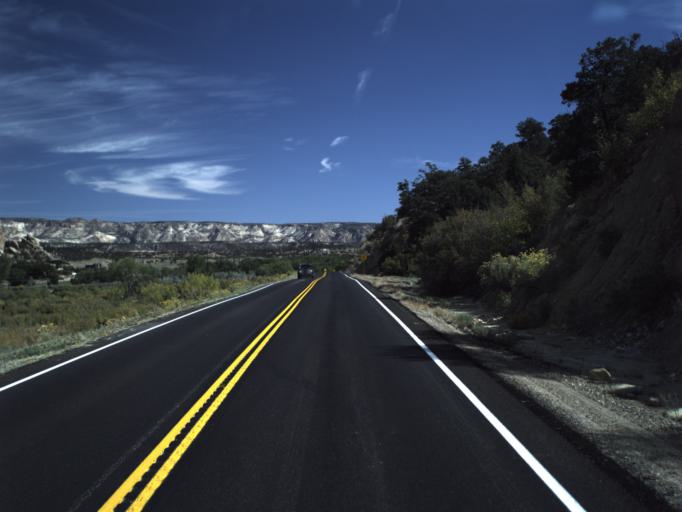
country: US
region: Utah
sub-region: Wayne County
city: Loa
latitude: 37.7633
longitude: -111.6878
